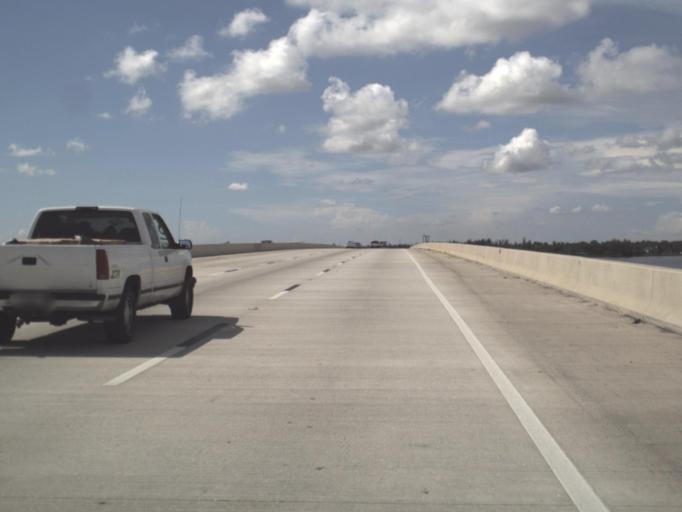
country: US
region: Florida
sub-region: Charlotte County
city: Harbour Heights
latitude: 26.9613
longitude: -82.0202
